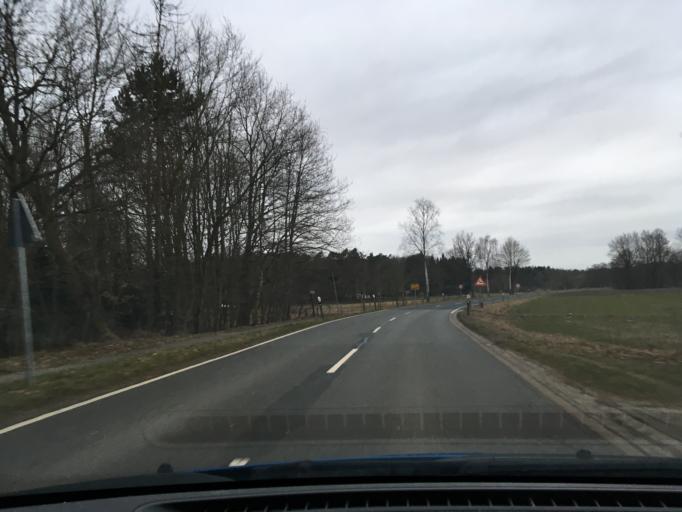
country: DE
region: Lower Saxony
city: Barum
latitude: 53.3359
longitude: 10.3975
